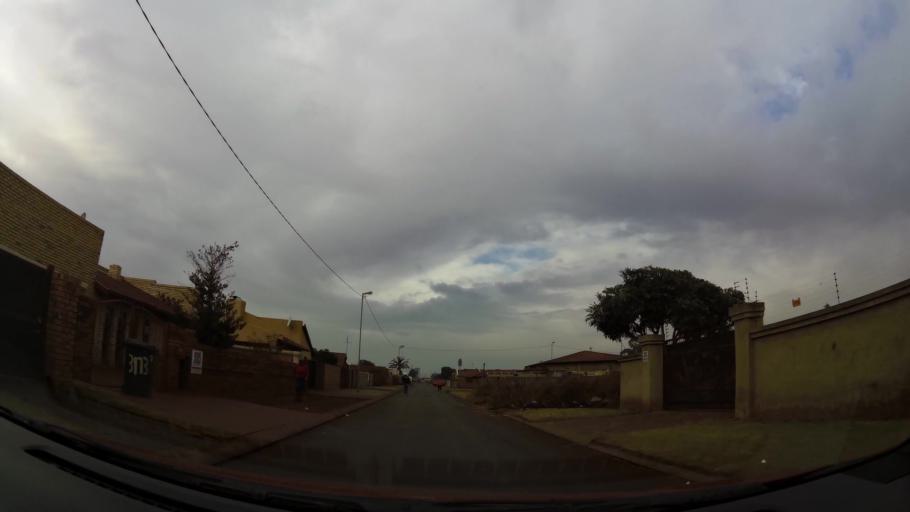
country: ZA
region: Gauteng
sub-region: City of Johannesburg Metropolitan Municipality
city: Soweto
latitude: -26.2876
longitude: 27.8402
